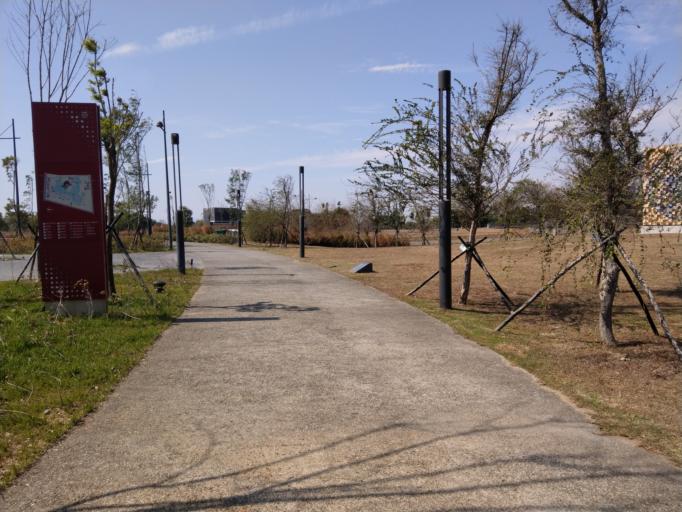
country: TW
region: Taiwan
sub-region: Chiayi
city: Taibao
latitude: 23.4751
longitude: 120.2917
